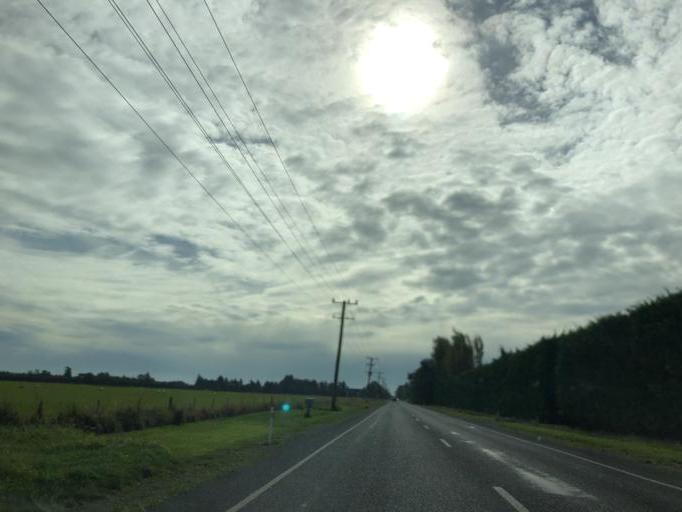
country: NZ
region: Canterbury
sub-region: Selwyn District
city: Lincoln
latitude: -43.6292
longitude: 172.4272
